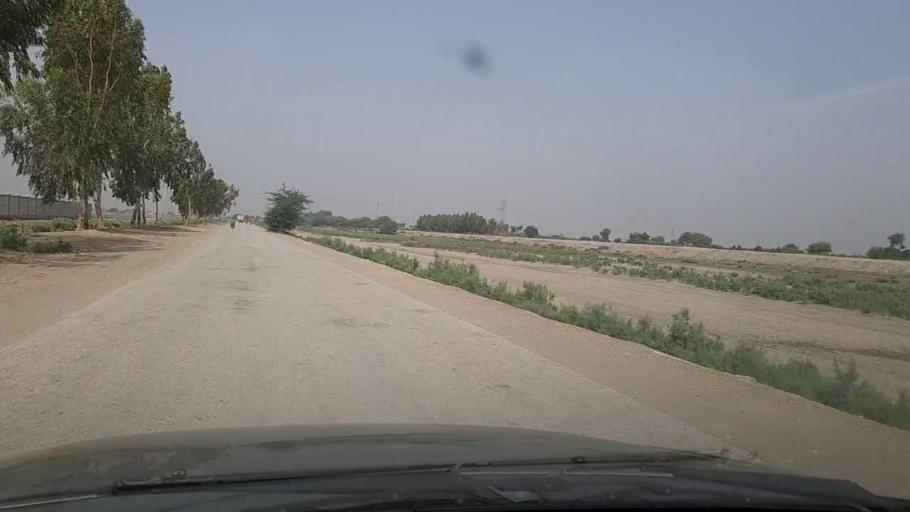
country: PK
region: Sindh
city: Thul
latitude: 28.3225
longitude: 68.7487
